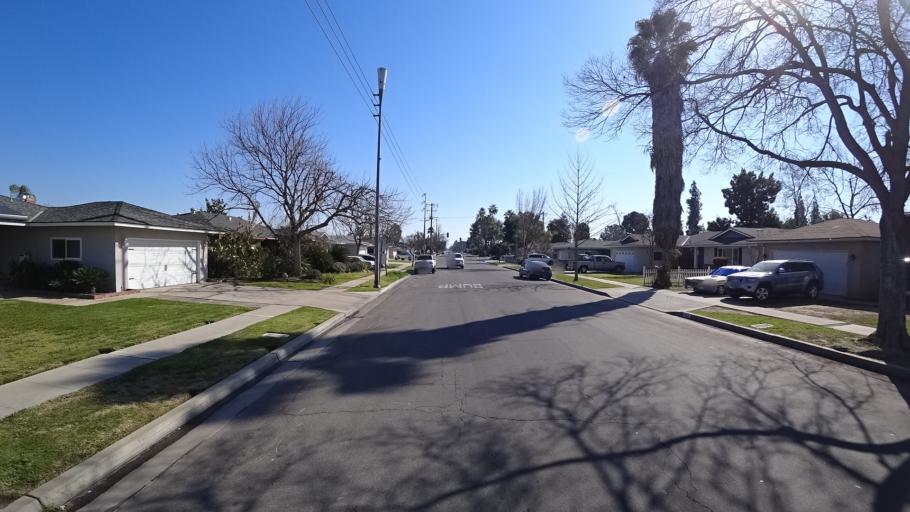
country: US
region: California
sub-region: Fresno County
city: Clovis
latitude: 36.8302
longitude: -119.7736
